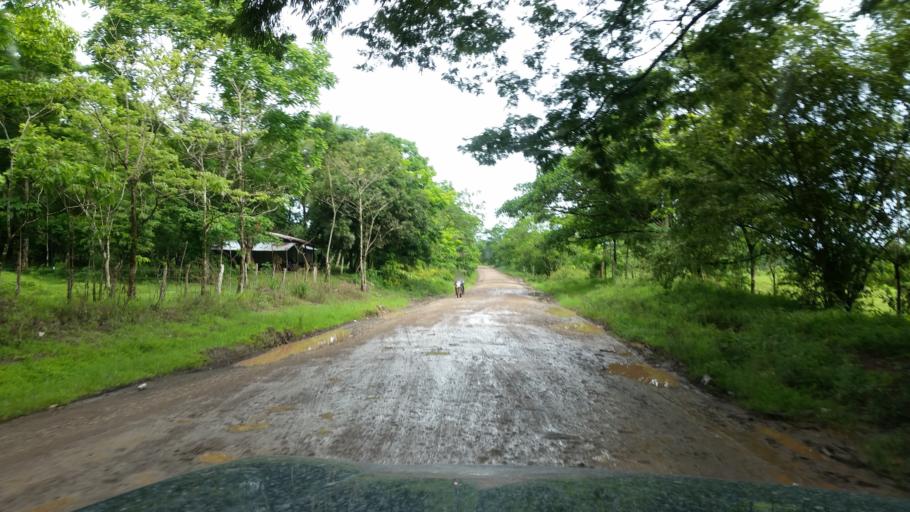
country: NI
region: Atlantico Norte (RAAN)
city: Siuna
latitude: 13.4259
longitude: -84.8528
